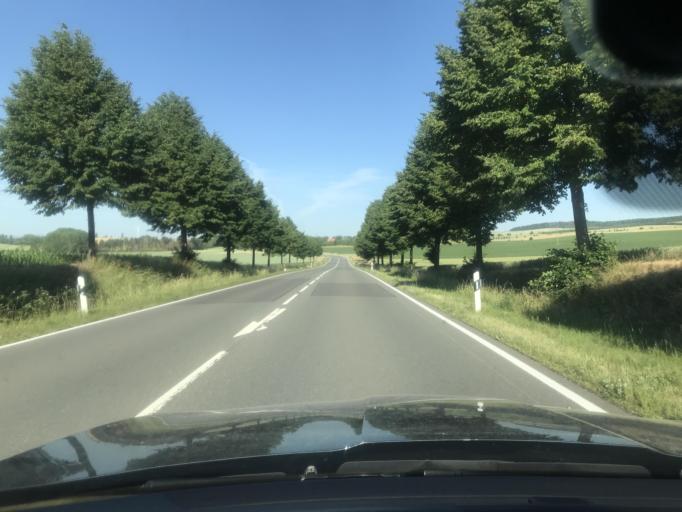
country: DE
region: Saxony-Anhalt
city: Strobeck
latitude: 51.9357
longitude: 10.9342
